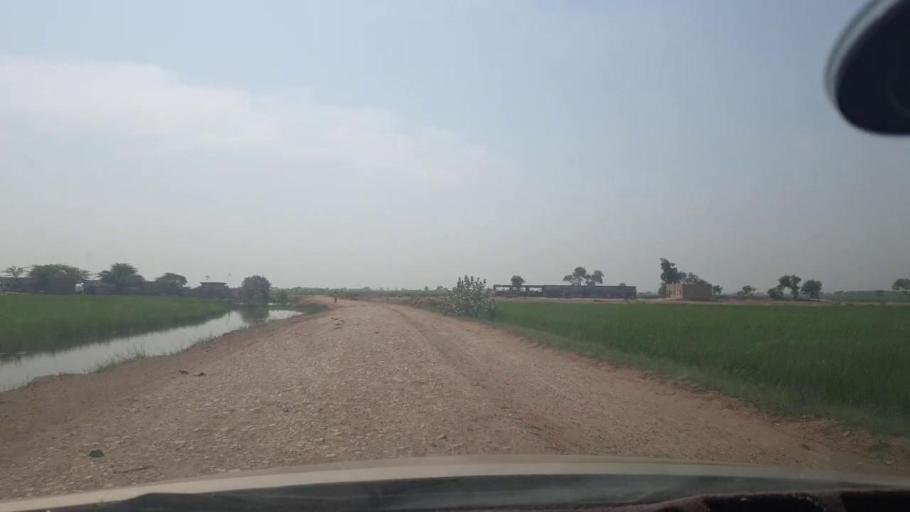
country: PK
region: Sindh
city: Jacobabad
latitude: 28.2710
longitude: 68.5120
